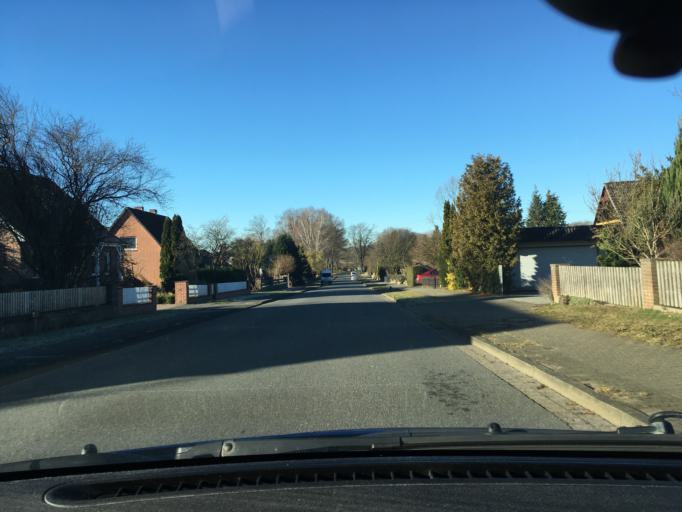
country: DE
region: Lower Saxony
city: Melbeck
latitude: 53.1774
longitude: 10.3947
